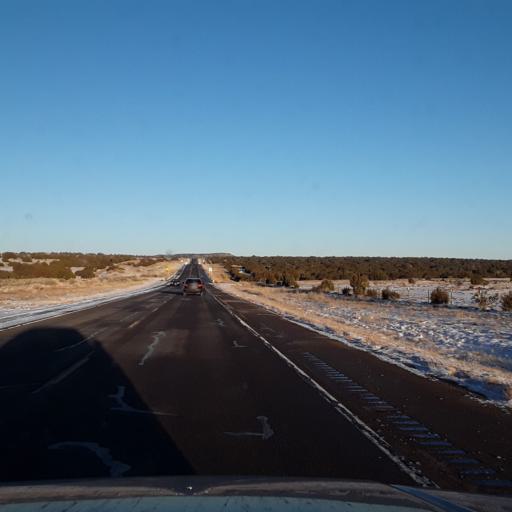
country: US
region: New Mexico
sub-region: Lincoln County
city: Carrizozo
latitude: 34.2304
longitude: -105.6297
